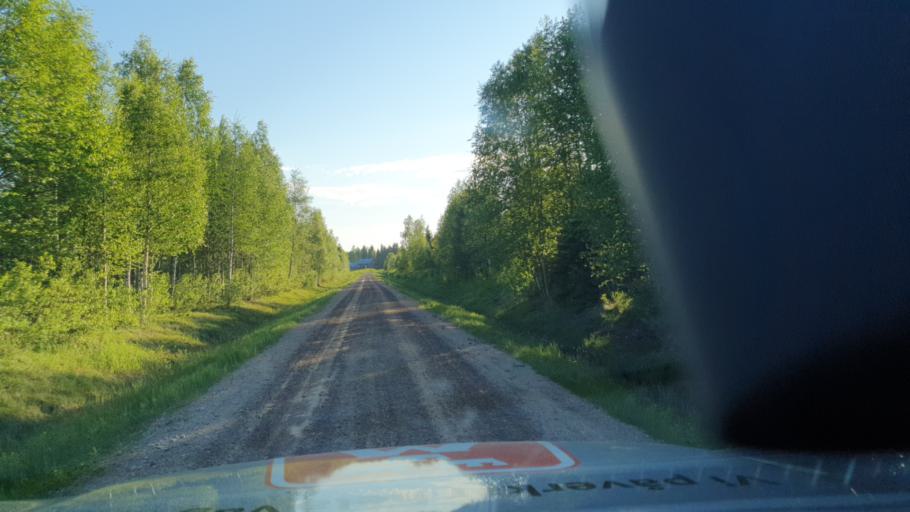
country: FI
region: Lapland
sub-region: Torniolaakso
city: Ylitornio
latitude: 66.1535
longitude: 23.6774
